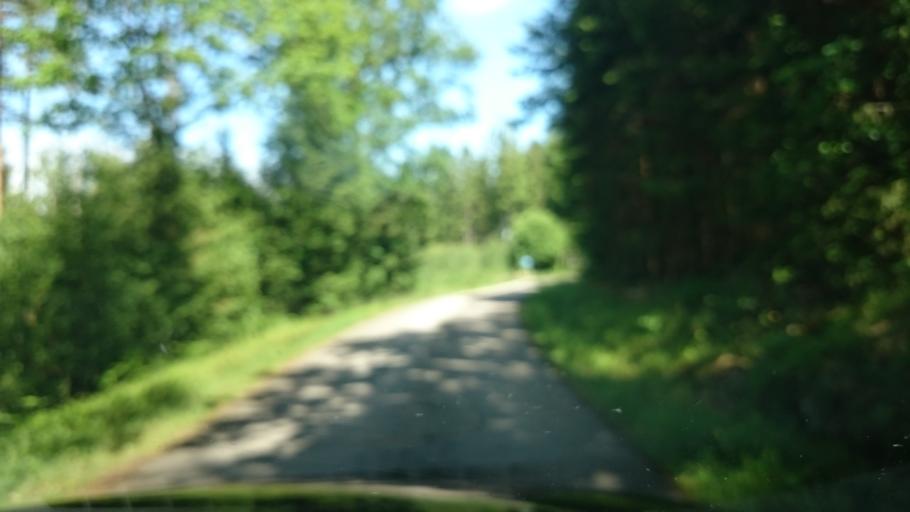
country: SE
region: Halland
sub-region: Hylte Kommun
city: Hyltebruk
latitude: 56.9614
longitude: 13.1849
